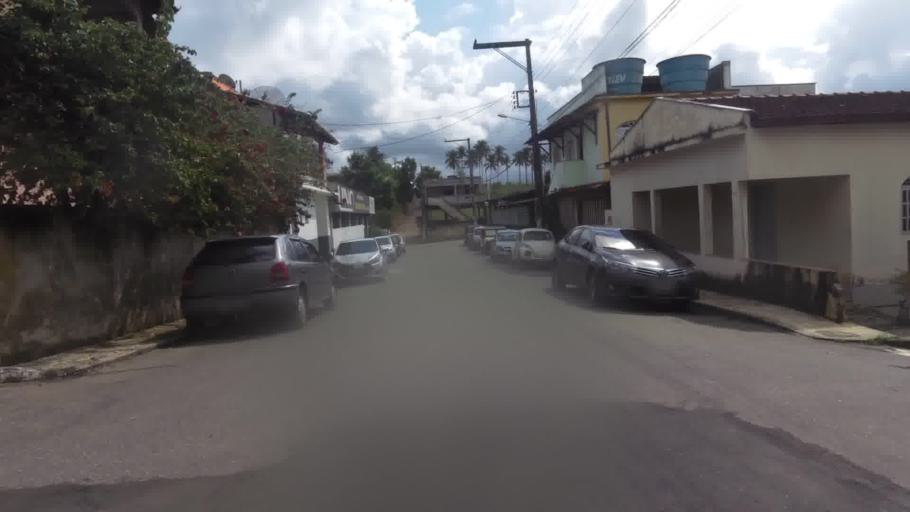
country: BR
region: Espirito Santo
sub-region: Piuma
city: Piuma
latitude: -20.8257
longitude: -40.6974
